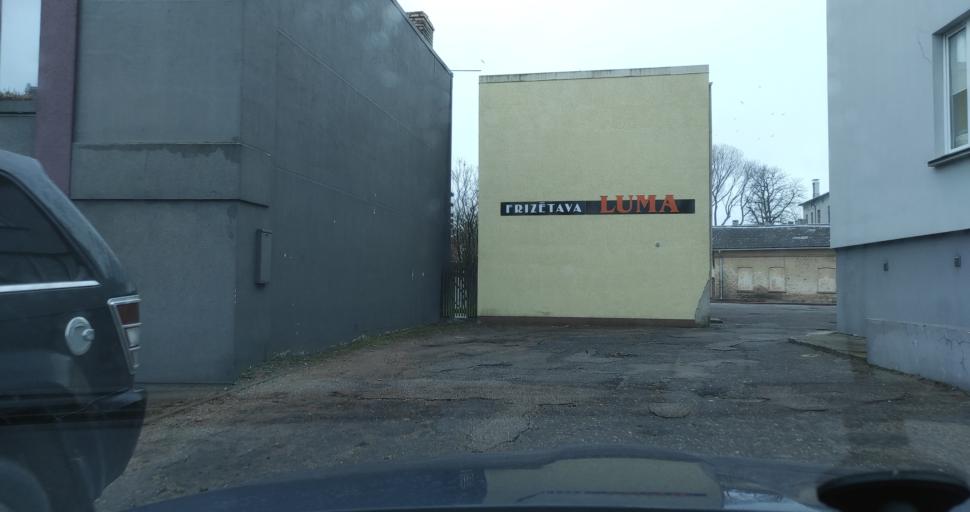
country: LV
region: Ventspils
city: Ventspils
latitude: 57.3945
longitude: 21.5690
